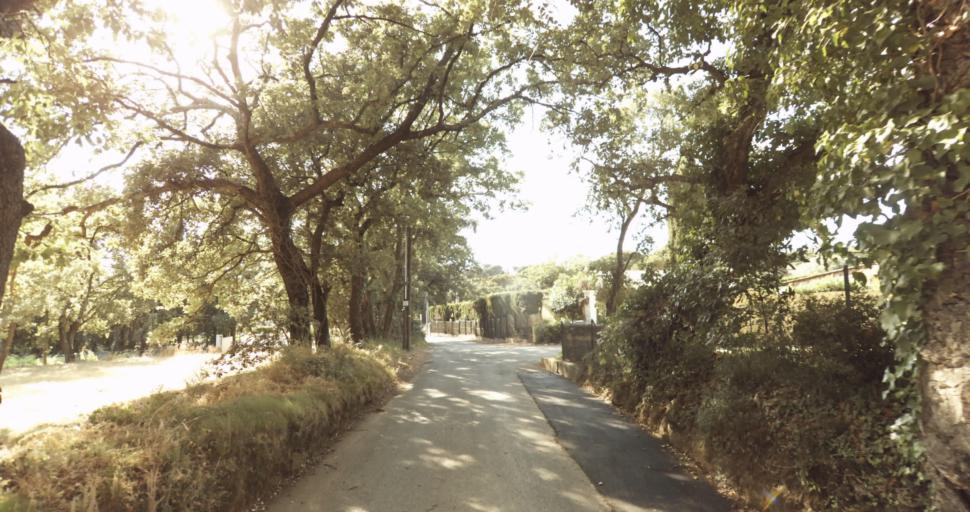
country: FR
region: Provence-Alpes-Cote d'Azur
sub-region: Departement du Var
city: Gassin
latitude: 43.2307
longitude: 6.5760
